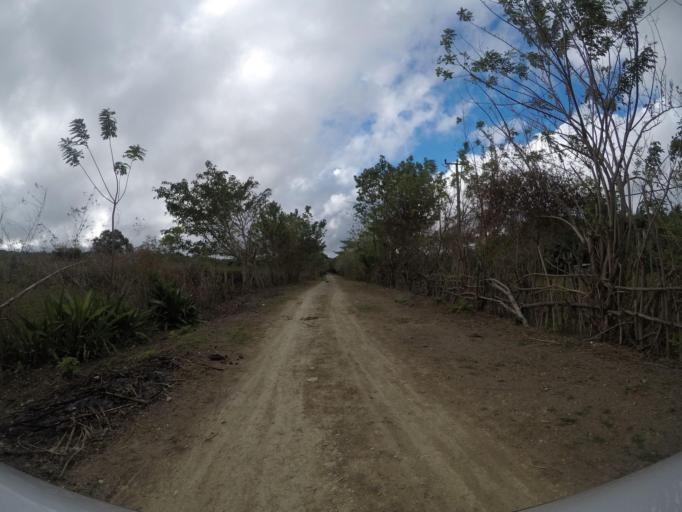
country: TL
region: Lautem
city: Lospalos
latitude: -8.5162
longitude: 126.9945
